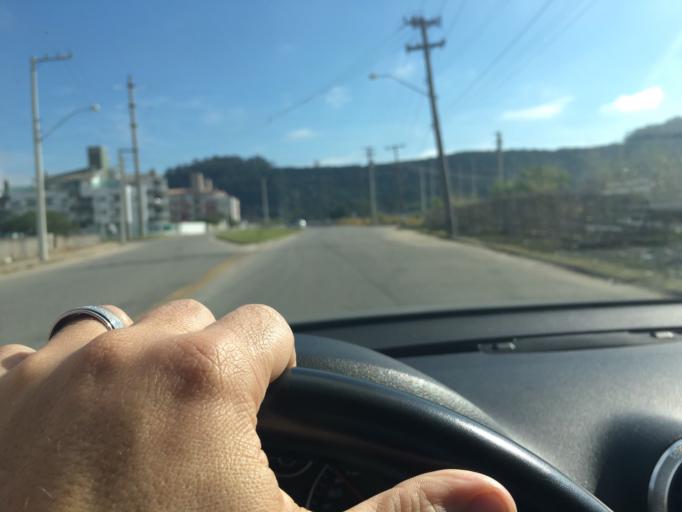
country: BR
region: Santa Catarina
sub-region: Florianopolis
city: Itacorubi
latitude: -27.4344
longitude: -48.4061
